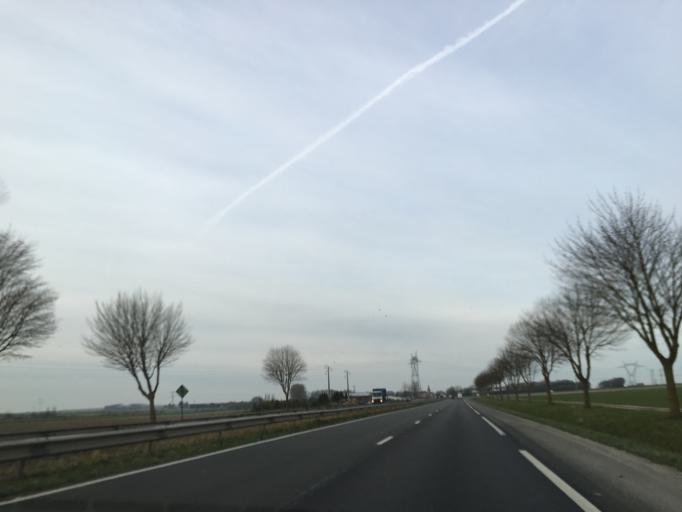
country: FR
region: Nord-Pas-de-Calais
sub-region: Departement du Pas-de-Calais
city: Roeux
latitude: 50.3327
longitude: 2.9060
